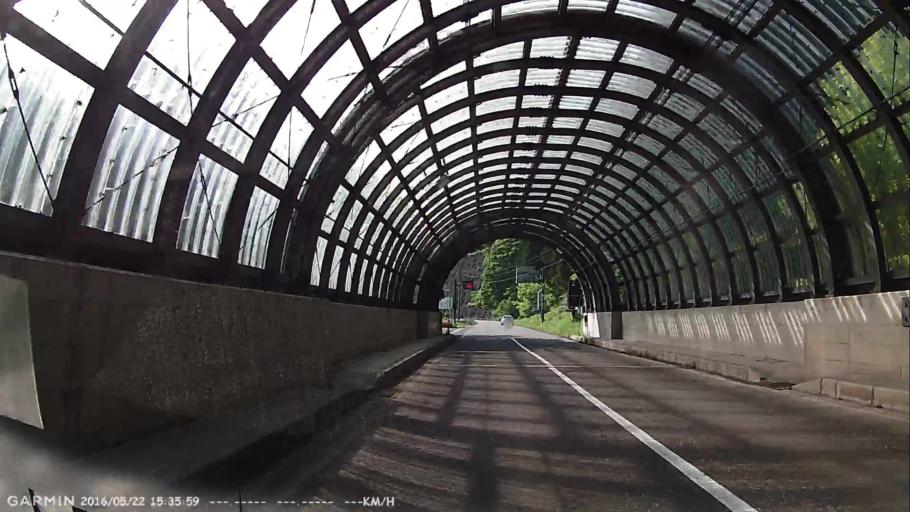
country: JP
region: Fukushima
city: Inawashiro
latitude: 37.2849
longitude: 139.9675
